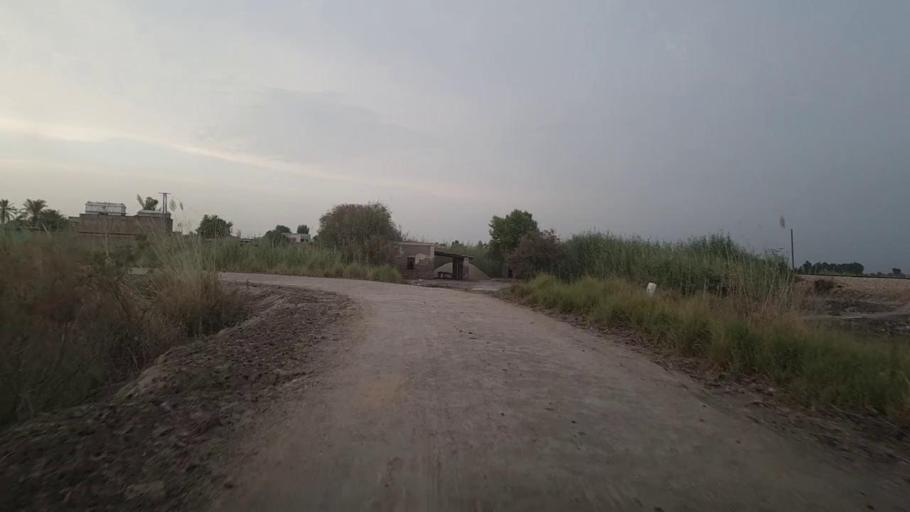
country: PK
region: Sindh
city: Karaundi
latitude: 27.0016
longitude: 68.3526
